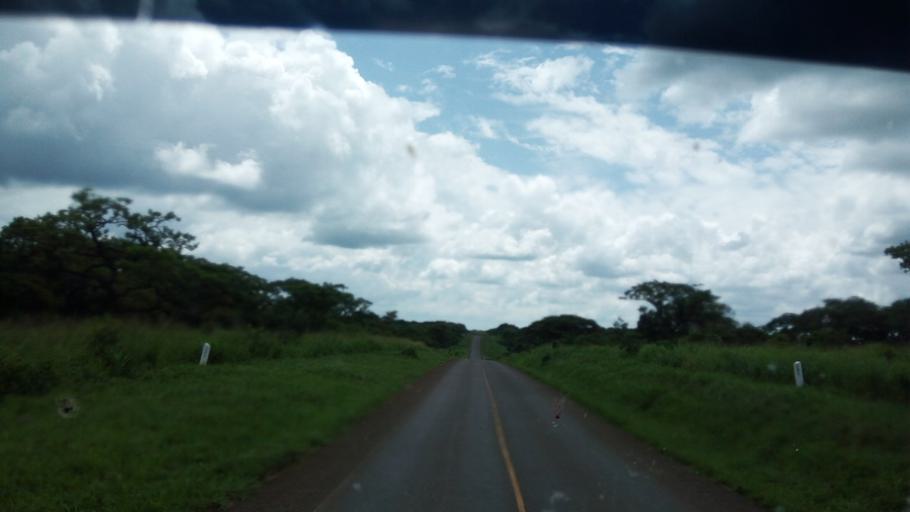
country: UG
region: Northern Region
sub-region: Oyam District
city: Oyam
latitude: 2.2958
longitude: 32.1966
